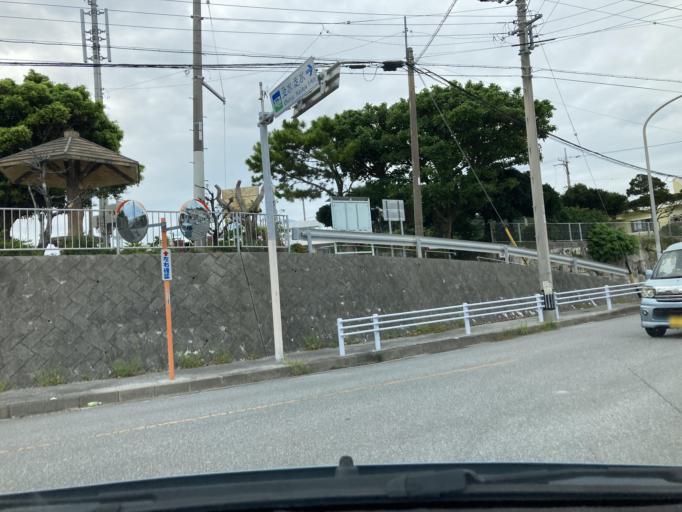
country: JP
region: Okinawa
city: Tomigusuku
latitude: 26.1410
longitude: 127.7916
